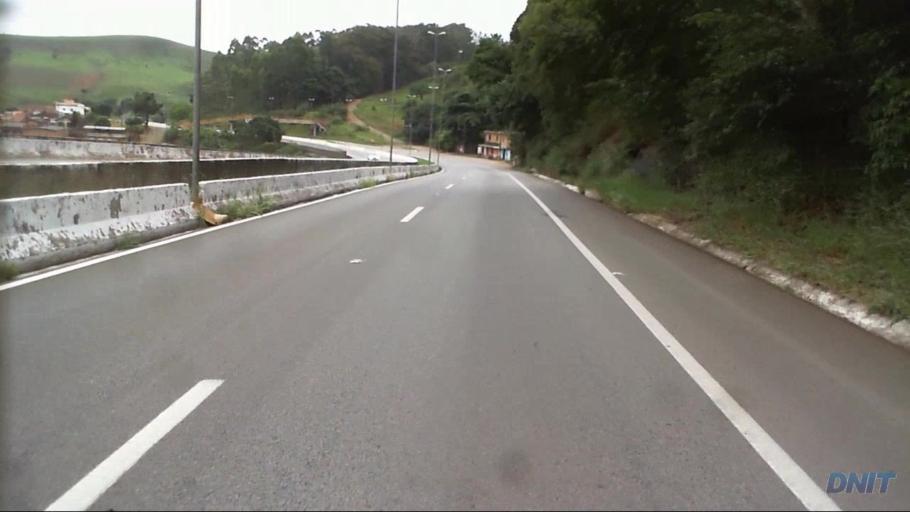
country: BR
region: Minas Gerais
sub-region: Nova Era
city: Nova Era
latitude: -19.7624
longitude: -43.0406
